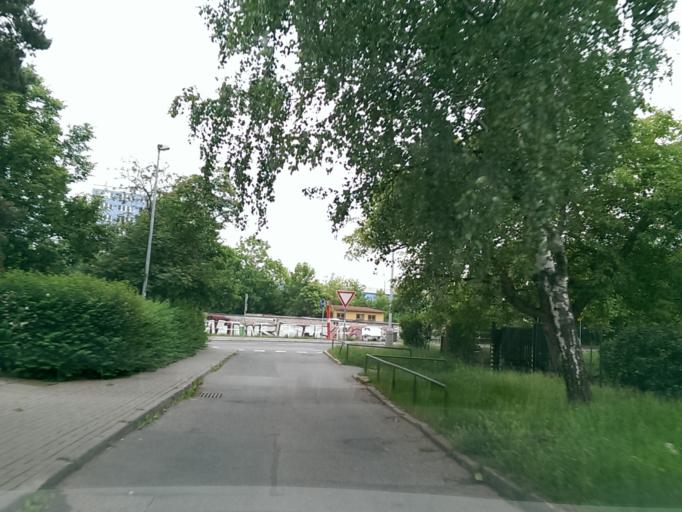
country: CZ
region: Praha
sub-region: Praha 8
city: Karlin
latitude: 50.0466
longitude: 14.4677
